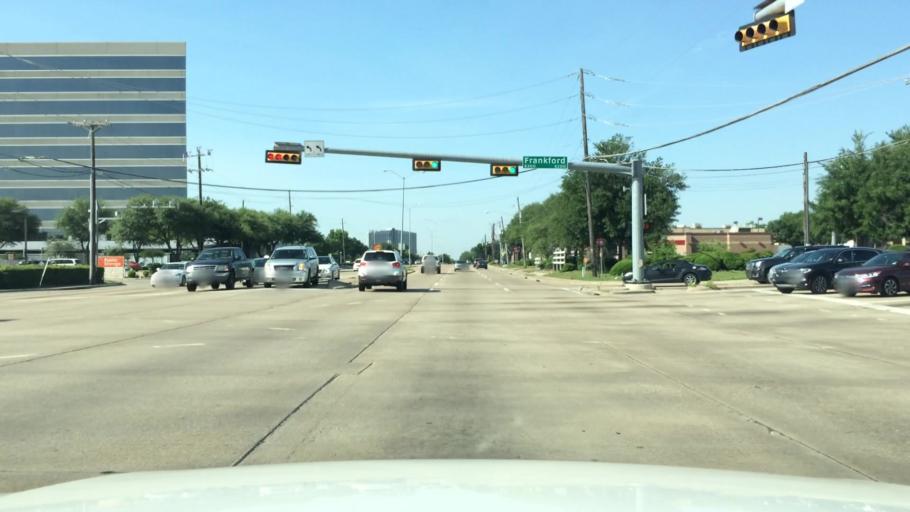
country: US
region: Texas
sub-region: Dallas County
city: Addison
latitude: 32.9985
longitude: -96.7977
